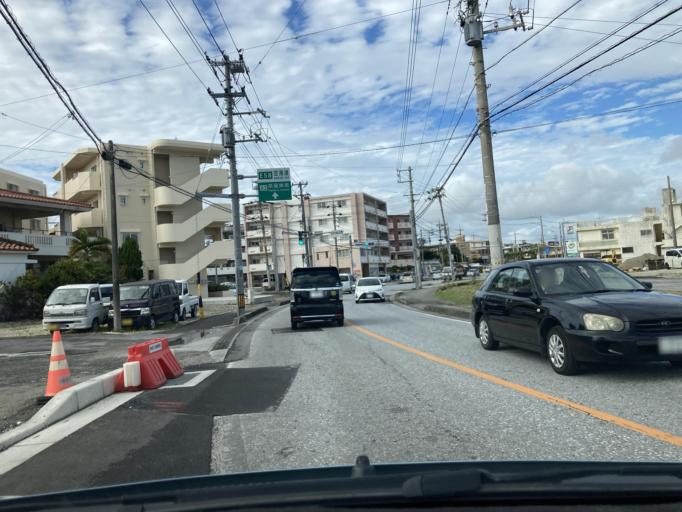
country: JP
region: Okinawa
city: Tomigusuku
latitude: 26.1526
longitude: 127.7213
